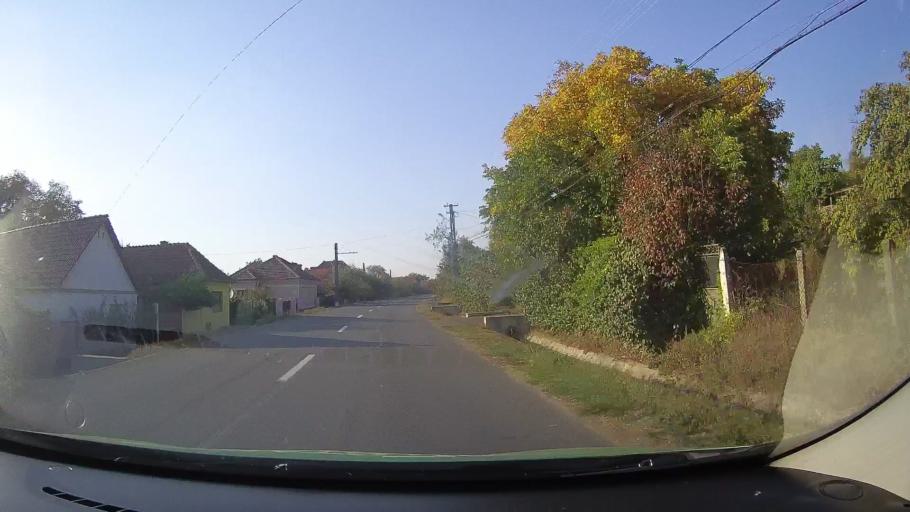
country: RO
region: Arad
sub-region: Comuna Ghioroc
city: Ghioroc
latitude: 46.1459
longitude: 21.5978
